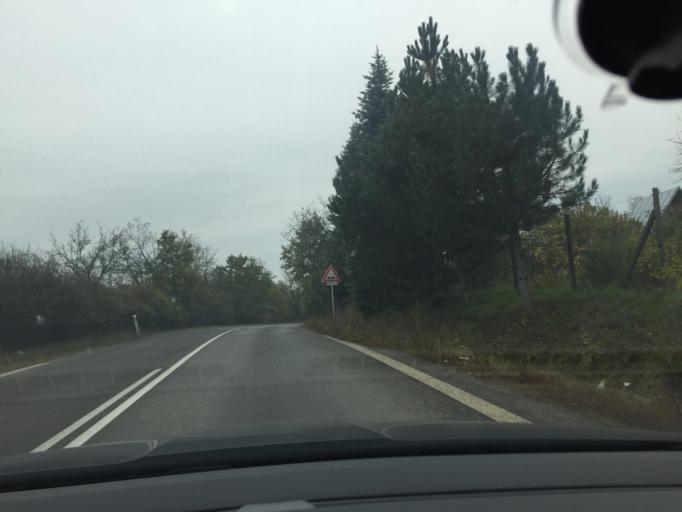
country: SK
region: Banskobystricky
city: Velky Krtis
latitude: 48.2173
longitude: 19.3696
